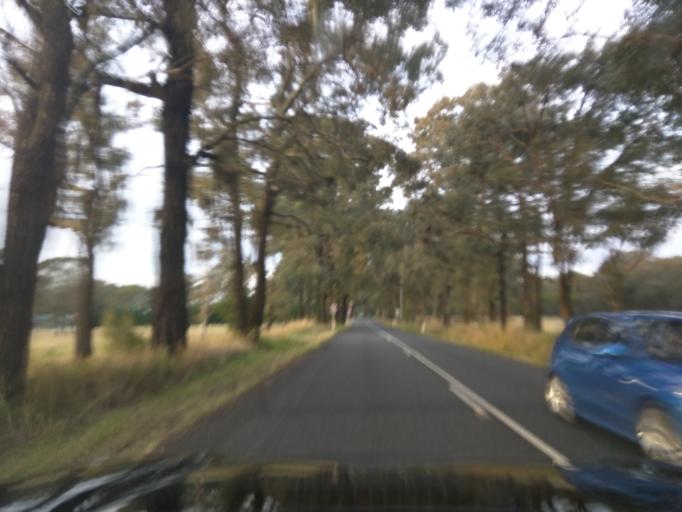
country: AU
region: New South Wales
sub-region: Wollondilly
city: Douglas Park
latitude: -34.2342
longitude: 150.7337
